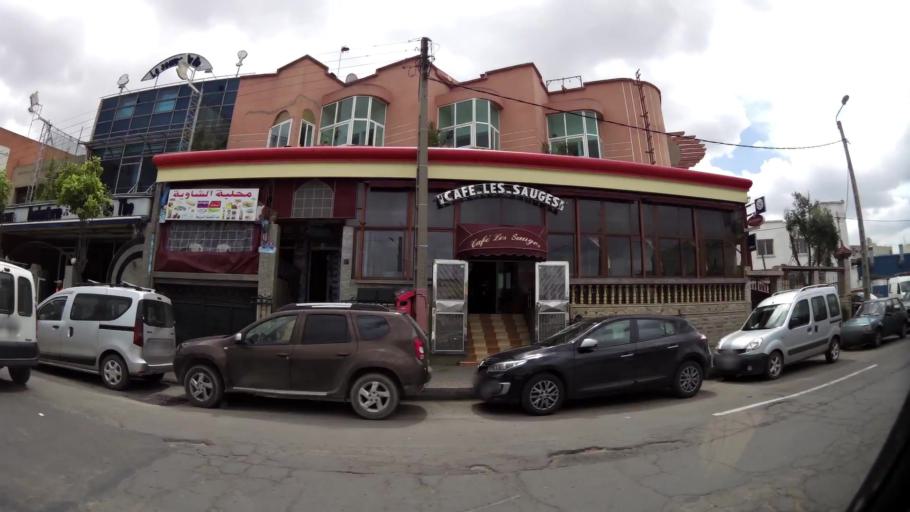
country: MA
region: Grand Casablanca
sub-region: Casablanca
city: Casablanca
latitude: 33.6026
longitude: -7.5437
